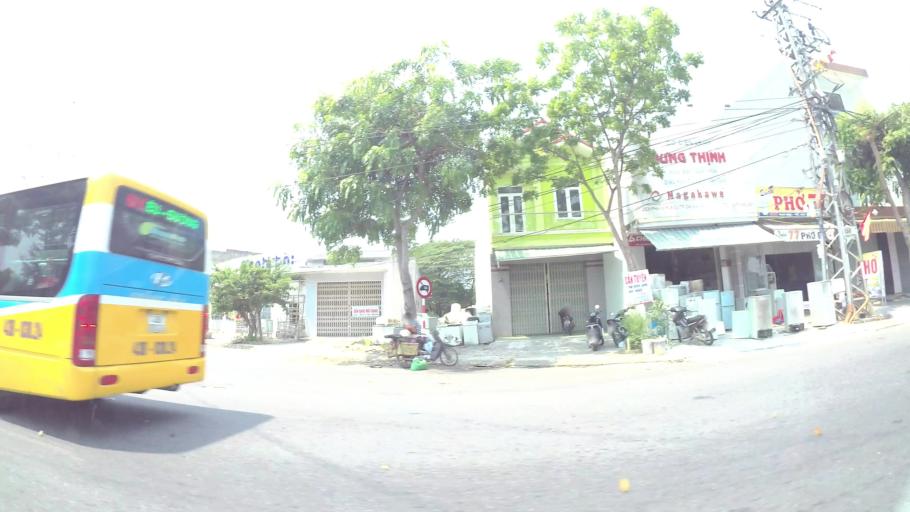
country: VN
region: Da Nang
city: Cam Le
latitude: 15.9971
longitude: 108.2073
